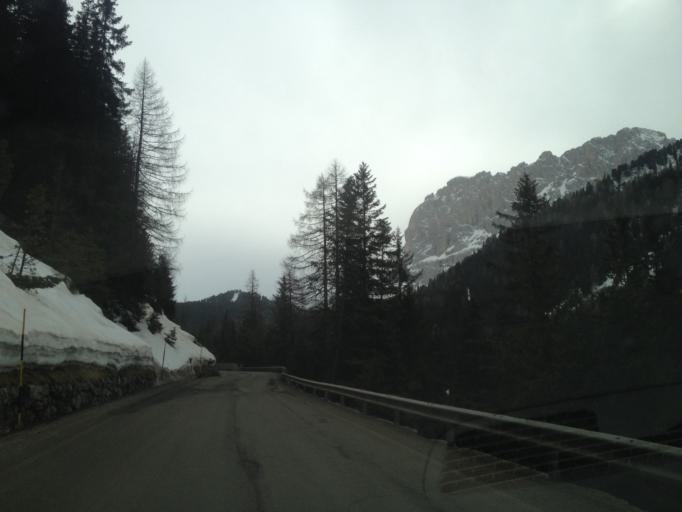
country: IT
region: Trentino-Alto Adige
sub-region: Bolzano
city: Selva
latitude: 46.5432
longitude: 11.7726
